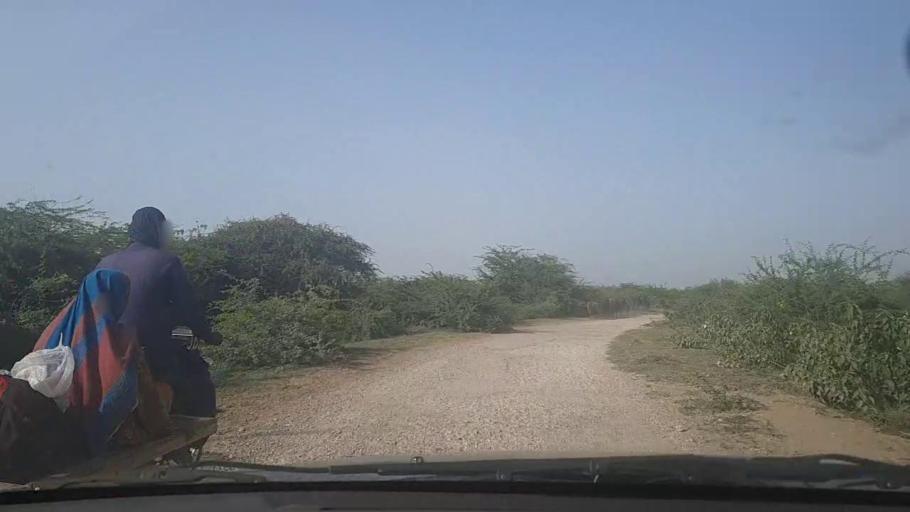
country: PK
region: Sindh
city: Keti Bandar
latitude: 24.2639
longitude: 67.5659
